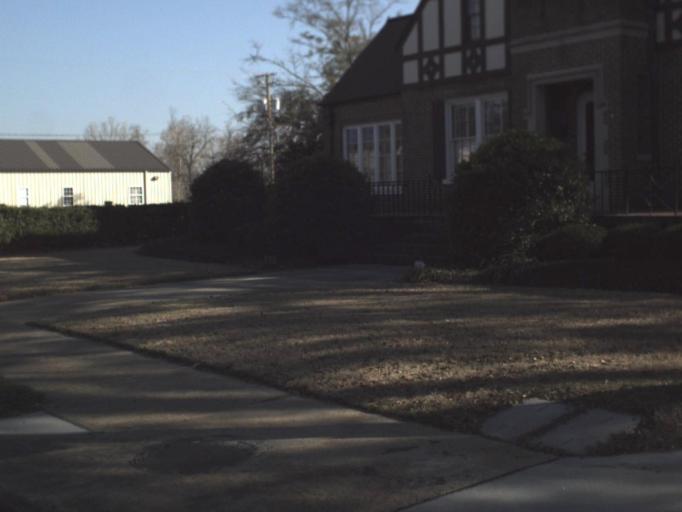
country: US
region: Florida
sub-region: Jackson County
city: Marianna
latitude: 30.7753
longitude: -85.2317
